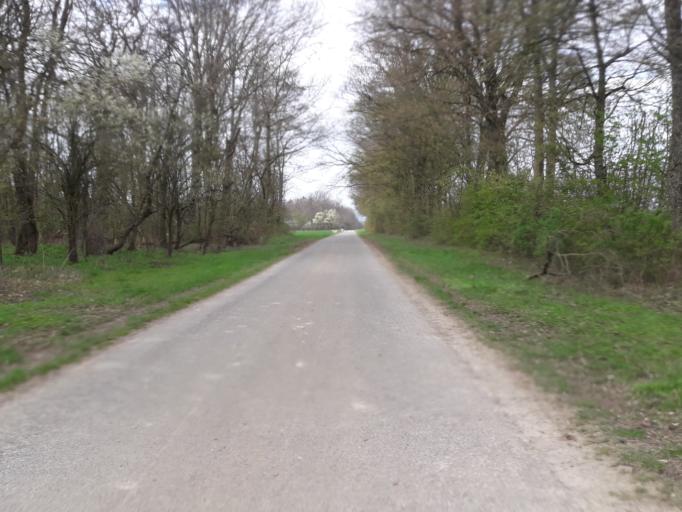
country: DE
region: North Rhine-Westphalia
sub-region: Regierungsbezirk Detmold
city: Paderborn
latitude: 51.6887
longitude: 8.7657
